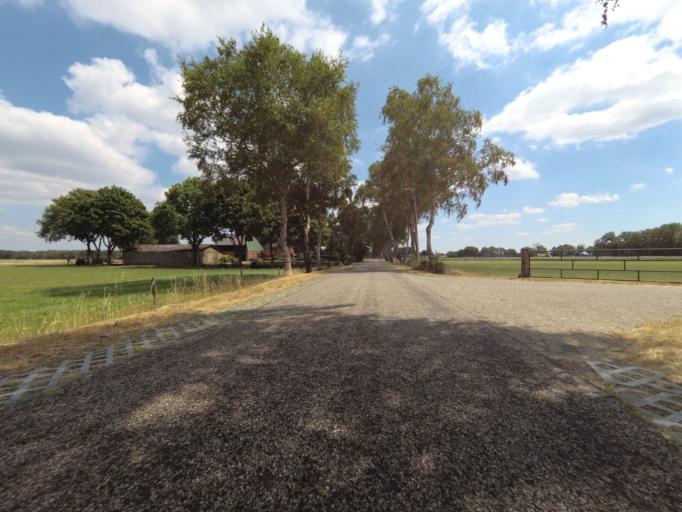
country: NL
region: Overijssel
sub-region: Gemeente Raalte
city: Raalte
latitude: 52.3285
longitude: 6.3551
